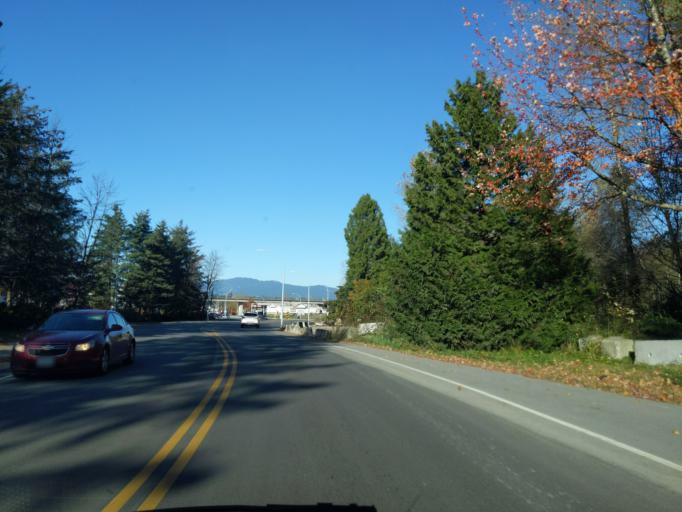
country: CA
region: British Columbia
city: New Westminster
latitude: 49.2033
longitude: -122.8678
